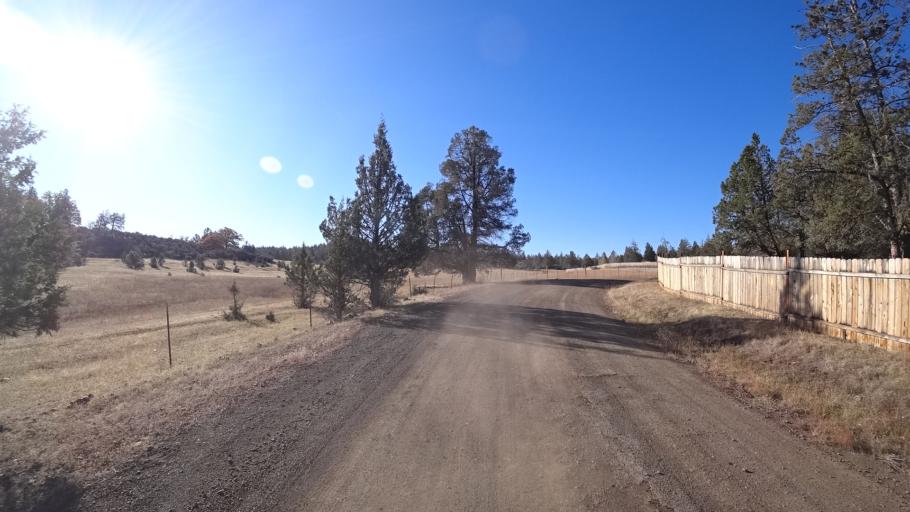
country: US
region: California
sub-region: Siskiyou County
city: Montague
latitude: 41.9169
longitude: -122.4228
